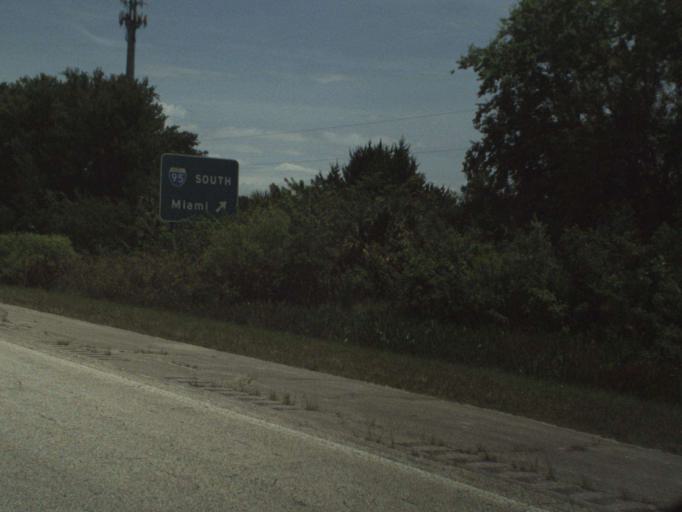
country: US
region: Florida
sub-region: Volusia County
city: South Daytona
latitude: 29.1537
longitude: -81.0794
